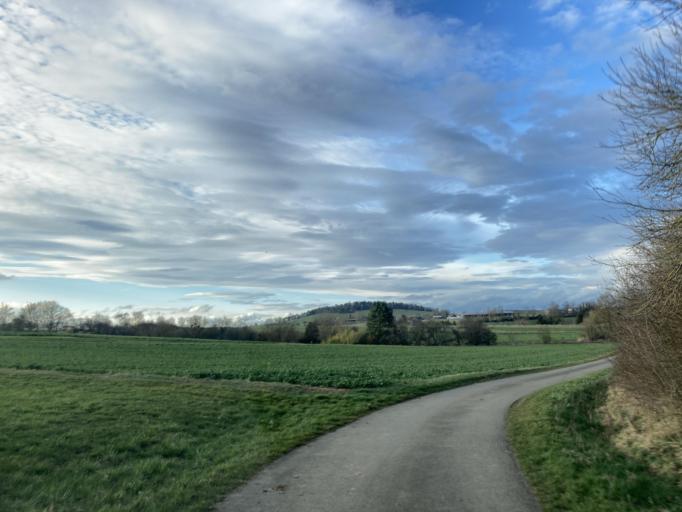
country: DE
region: Baden-Wuerttemberg
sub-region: Tuebingen Region
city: Rottenburg
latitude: 48.4806
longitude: 8.9081
